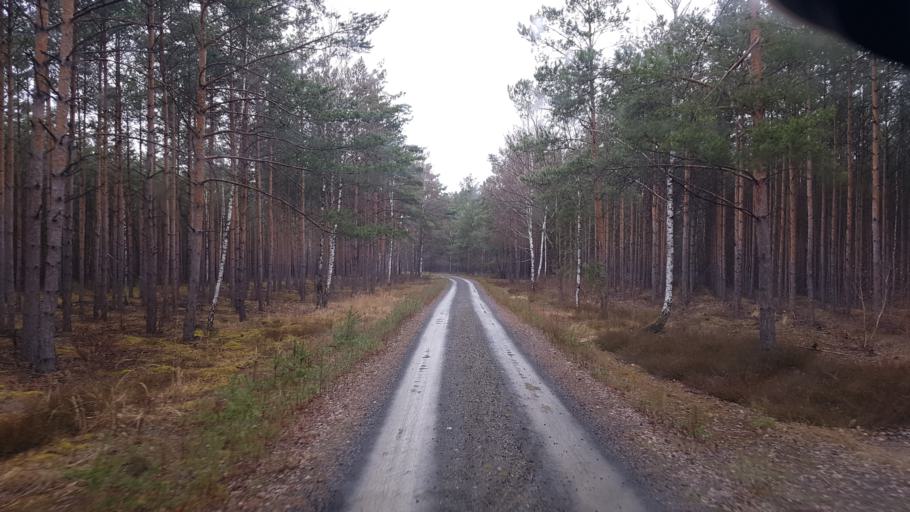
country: DE
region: Brandenburg
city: Grossraschen
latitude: 51.6171
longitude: 13.9763
